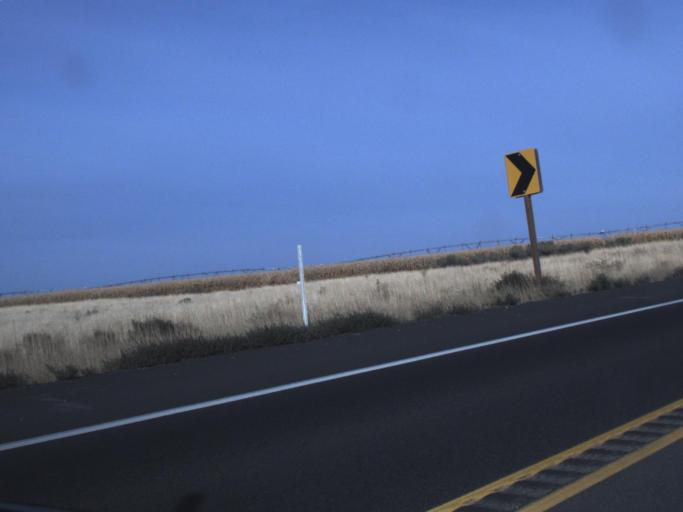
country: US
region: Oregon
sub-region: Umatilla County
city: Umatilla
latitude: 45.9582
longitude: -119.4093
